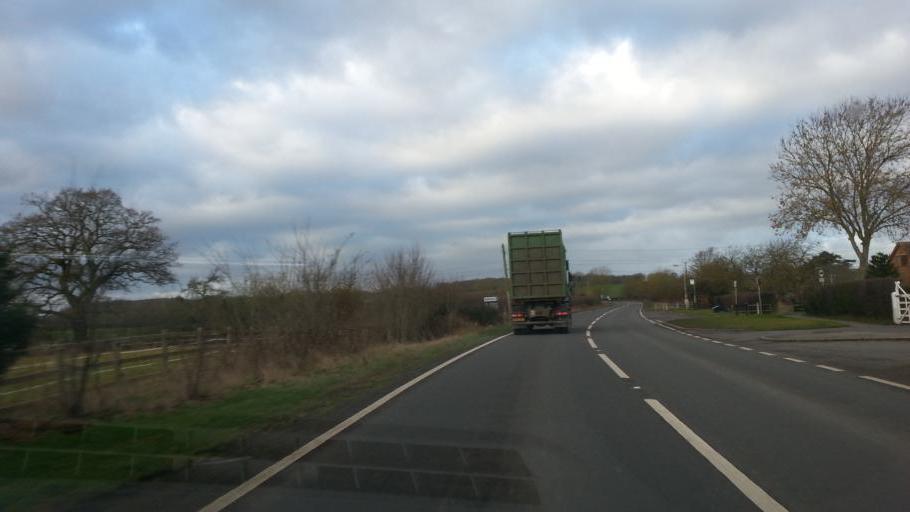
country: GB
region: England
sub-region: Nottinghamshire
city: Newark on Trent
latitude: 53.1059
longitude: -0.8380
